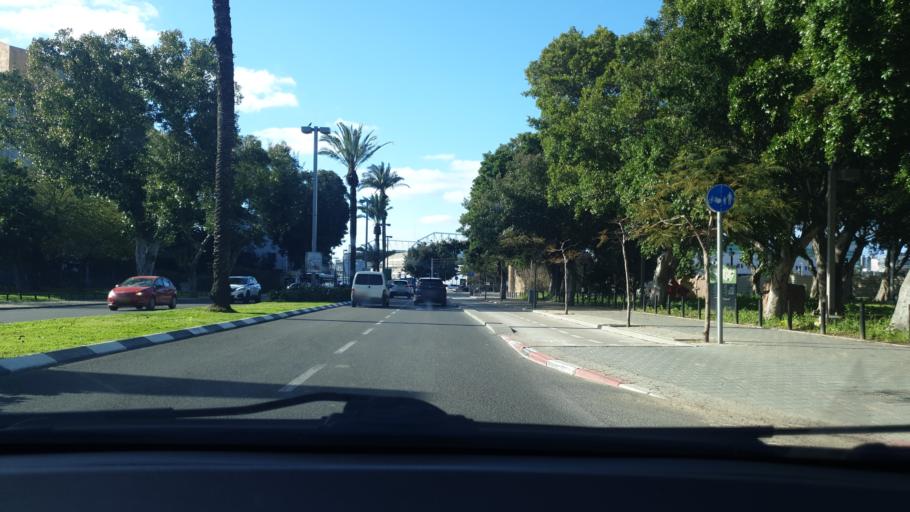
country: IL
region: Tel Aviv
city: Yafo
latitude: 32.0468
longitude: 34.7664
